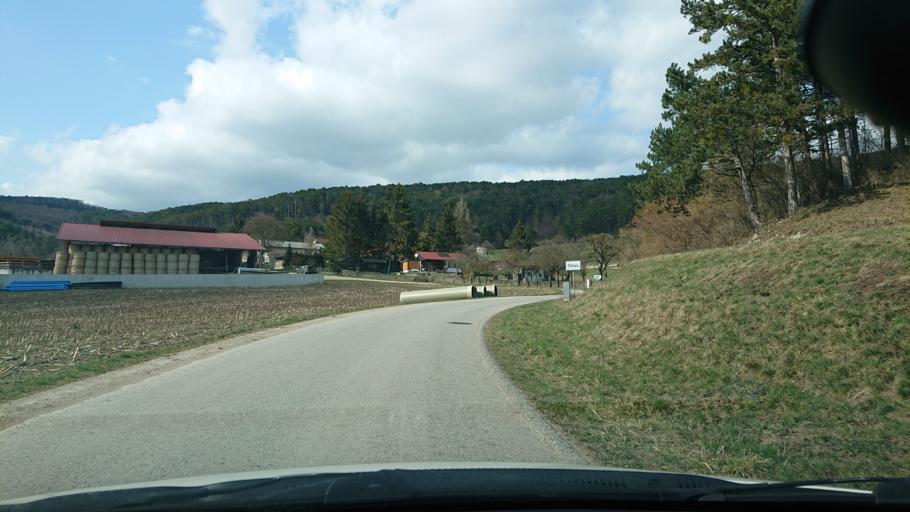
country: AT
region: Lower Austria
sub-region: Politischer Bezirk Baden
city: Pottenstein
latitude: 47.9426
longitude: 16.0679
